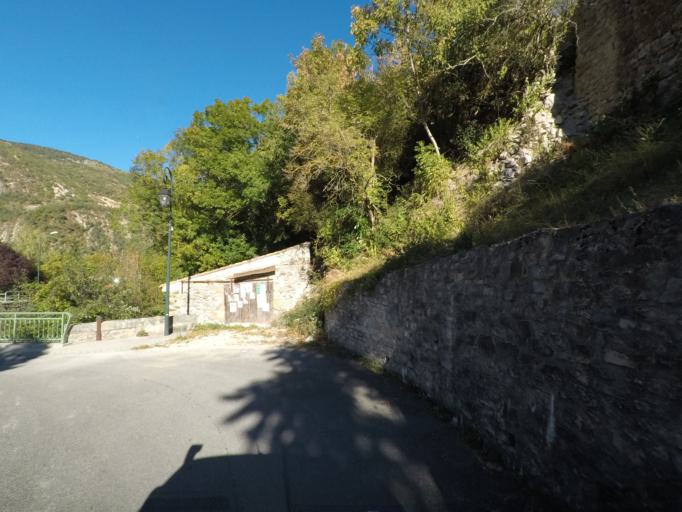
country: FR
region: Rhone-Alpes
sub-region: Departement de la Drome
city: Buis-les-Baronnies
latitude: 44.4709
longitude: 5.4513
